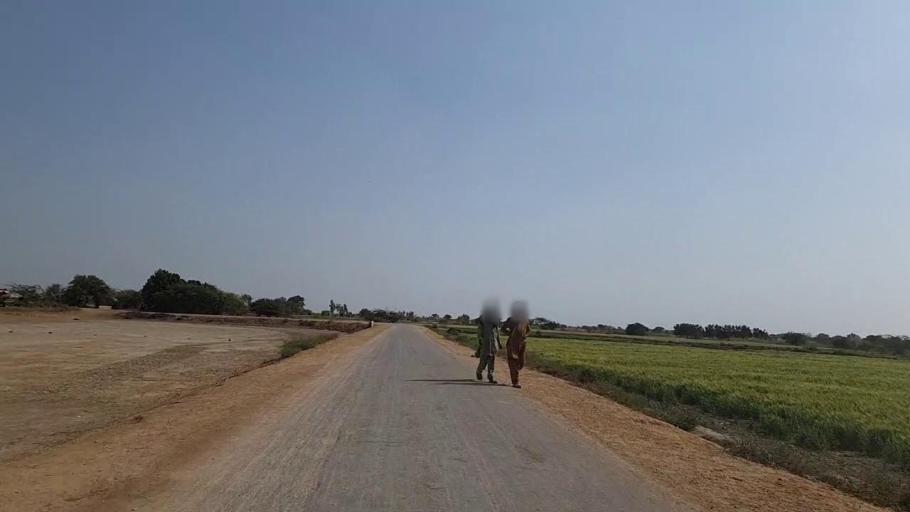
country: PK
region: Sindh
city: Daro Mehar
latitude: 24.7884
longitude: 68.1794
